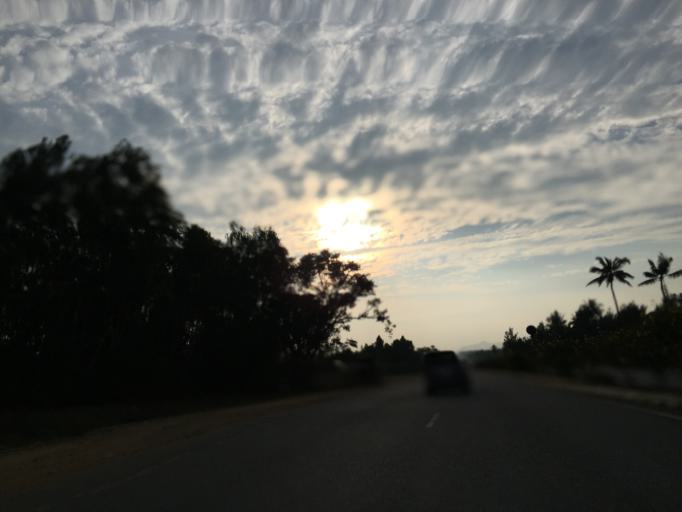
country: IN
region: Karnataka
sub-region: Kolar
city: Kolar
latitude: 13.1395
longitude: 78.2176
